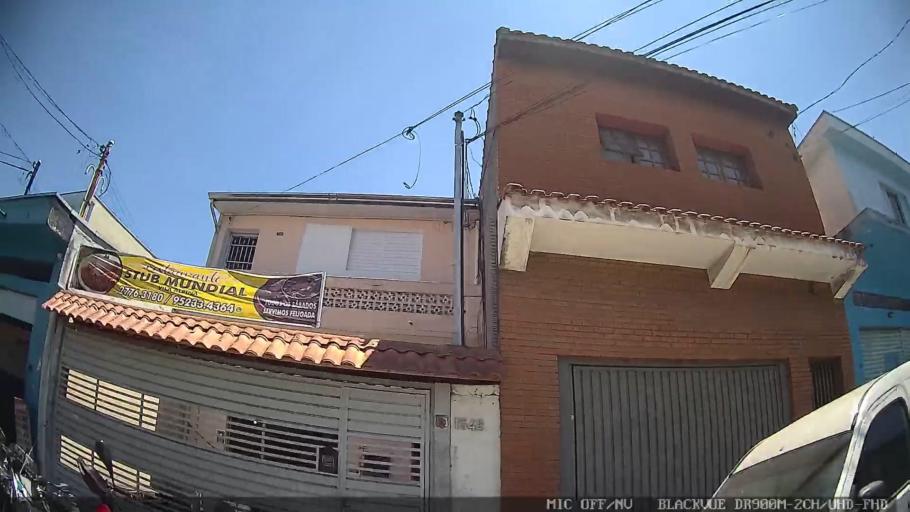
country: BR
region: Sao Paulo
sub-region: Sao Caetano Do Sul
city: Sao Caetano do Sul
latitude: -23.5989
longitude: -46.5525
